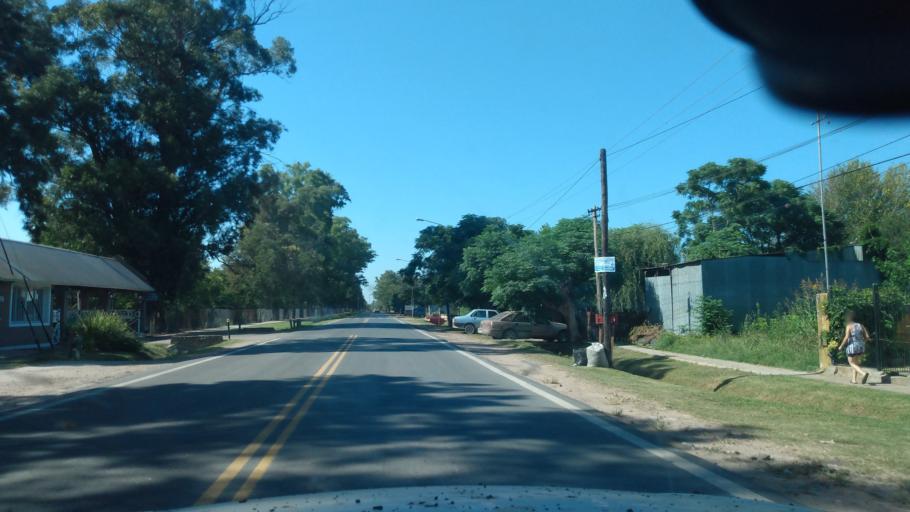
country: AR
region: Buenos Aires
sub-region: Partido de Lujan
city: Lujan
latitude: -34.4986
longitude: -59.0721
